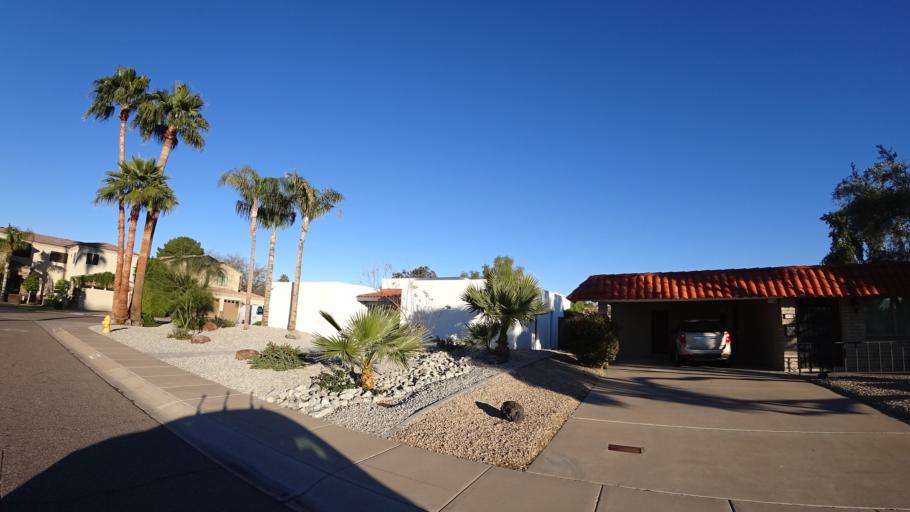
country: US
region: Arizona
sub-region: Maricopa County
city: Paradise Valley
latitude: 33.4934
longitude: -112.0071
